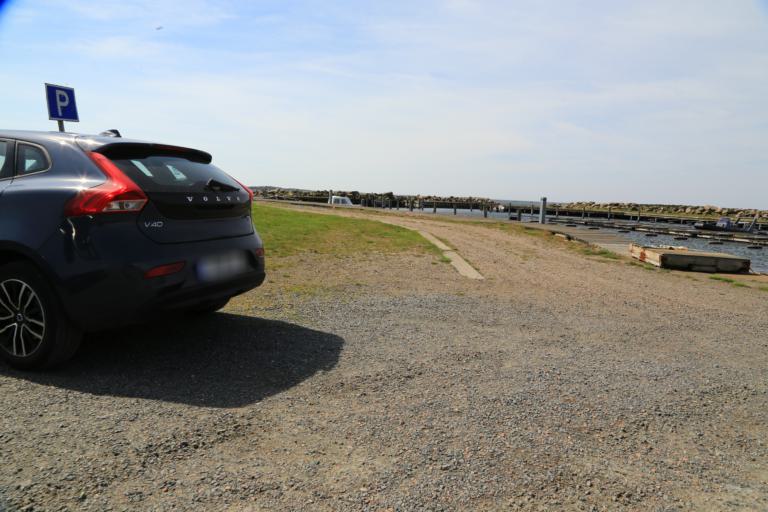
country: SE
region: Halland
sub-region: Varbergs Kommun
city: Varberg
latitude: 57.1407
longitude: 12.2165
